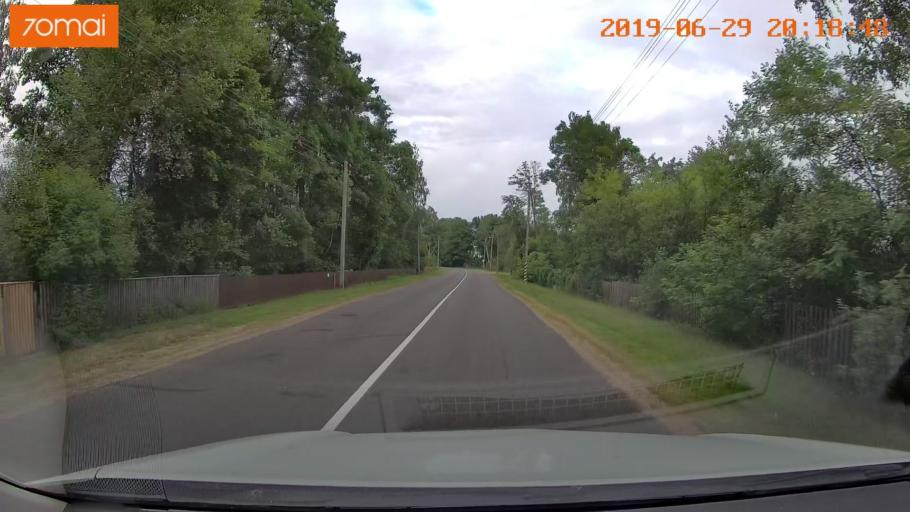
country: BY
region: Brest
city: Asnyezhytsy
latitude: 52.3962
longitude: 26.2402
